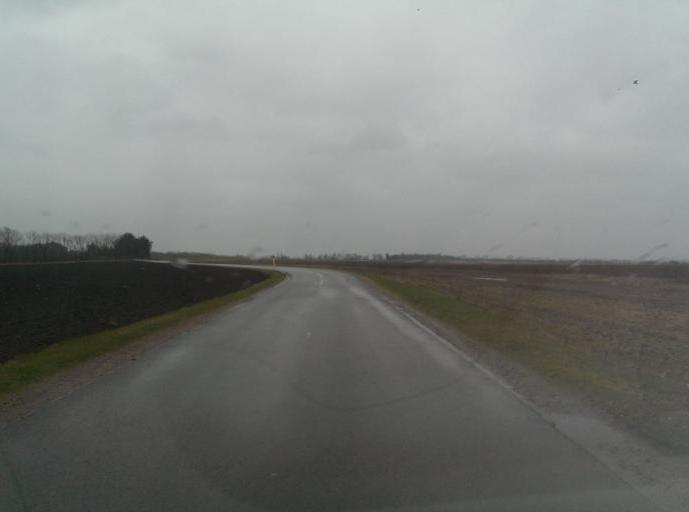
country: DK
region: Central Jutland
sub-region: Ringkobing-Skjern Kommune
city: Skjern
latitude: 56.0572
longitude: 8.4691
